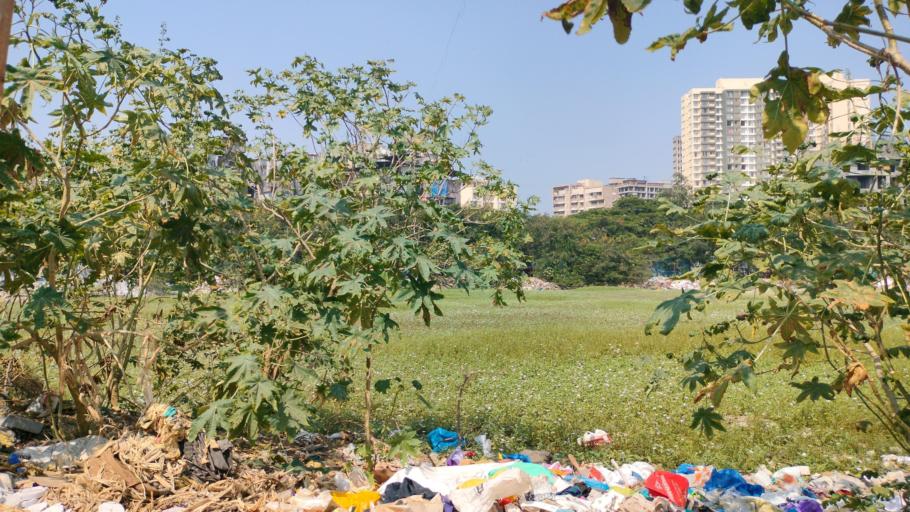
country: IN
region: Maharashtra
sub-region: Mumbai Suburban
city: Borivli
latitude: 19.2700
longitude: 72.8735
